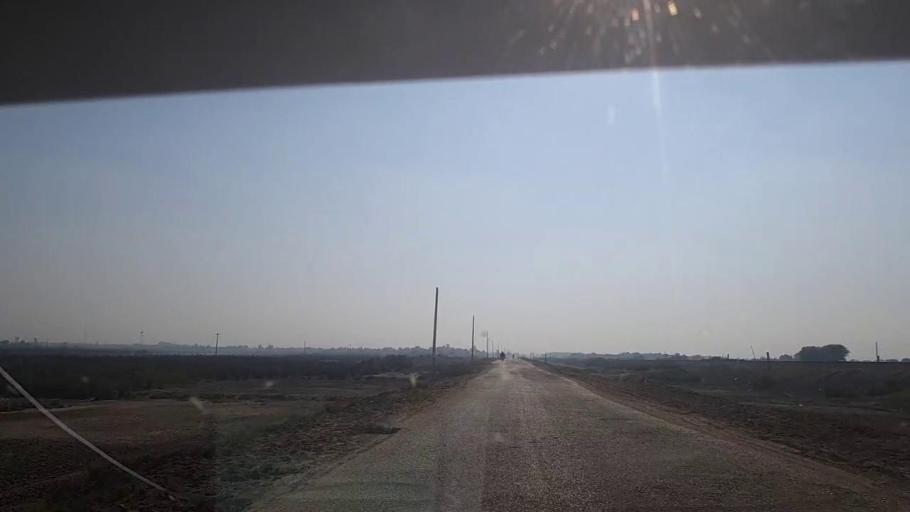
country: PK
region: Sindh
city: Gambat
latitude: 27.3583
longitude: 68.5538
